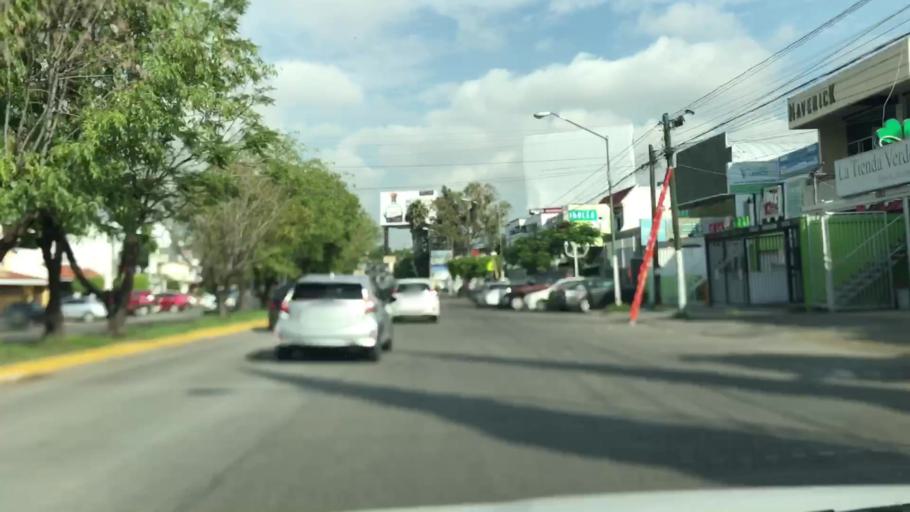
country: MX
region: Jalisco
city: Guadalajara
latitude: 20.6373
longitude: -103.4281
